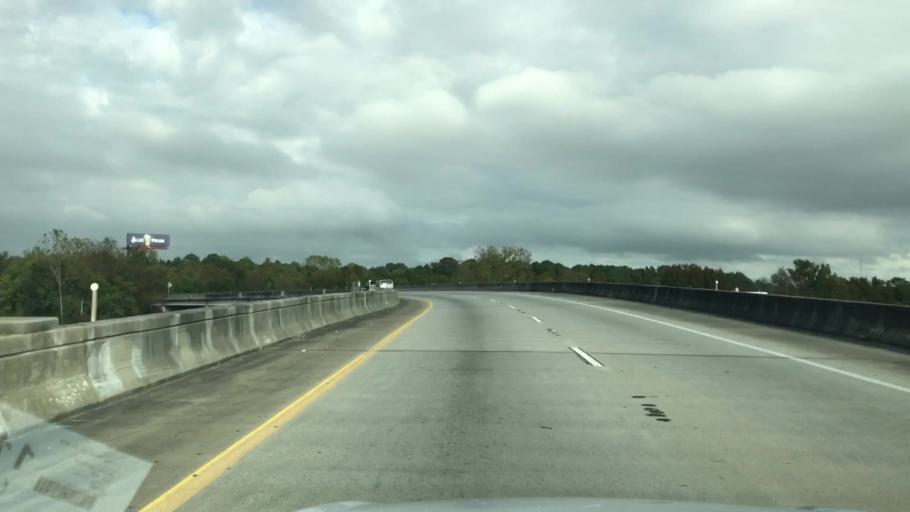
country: US
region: South Carolina
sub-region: Berkeley County
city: Hanahan
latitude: 32.8813
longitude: -80.0200
